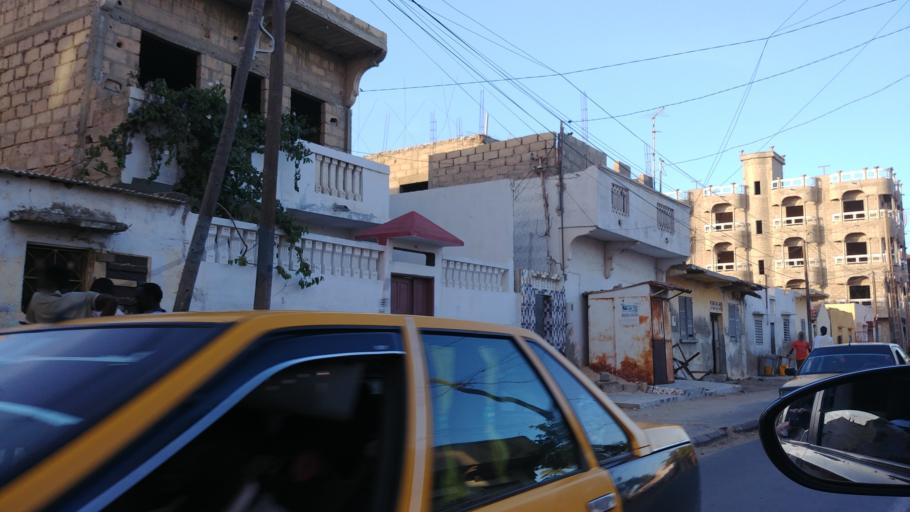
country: SN
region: Saint-Louis
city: Saint-Louis
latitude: 16.0249
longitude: -16.4948
